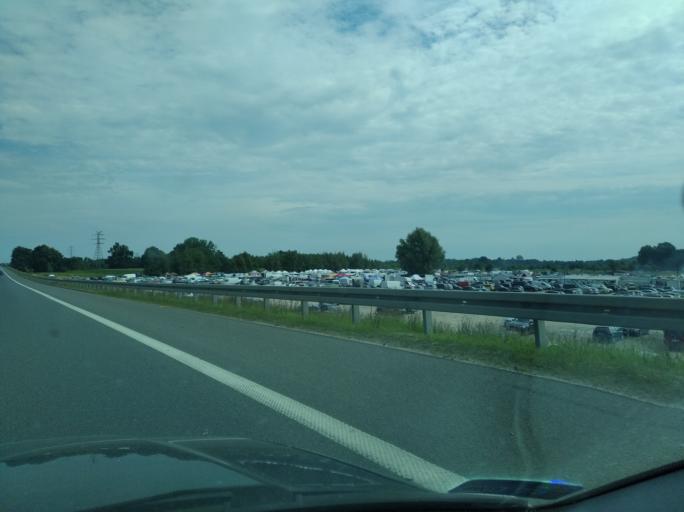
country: PL
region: Subcarpathian Voivodeship
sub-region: Powiat rzeszowski
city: Trzebownisko
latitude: 50.0688
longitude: 22.0556
